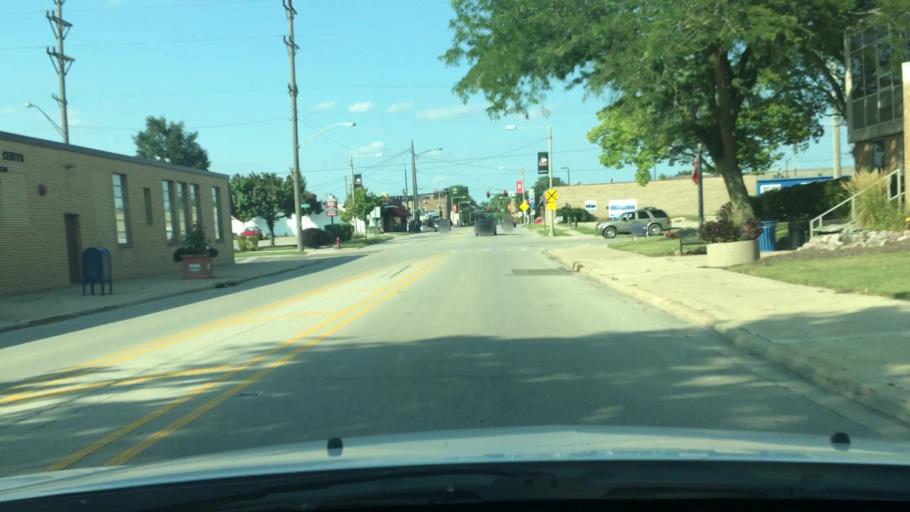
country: US
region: Illinois
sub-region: DeKalb County
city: DeKalb
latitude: 41.9281
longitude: -88.7508
